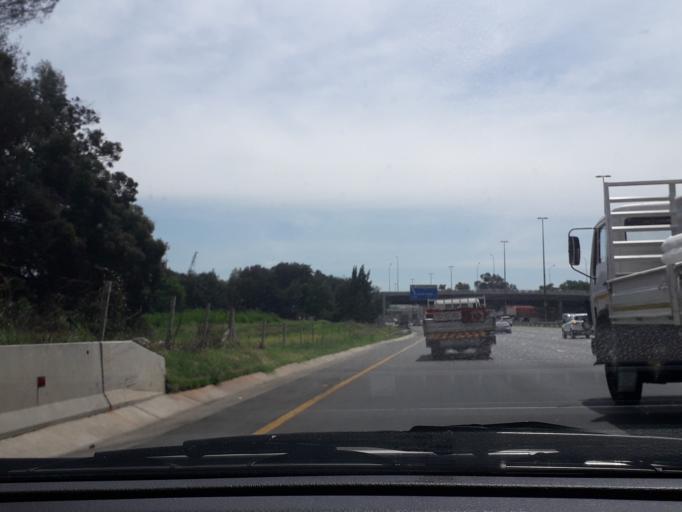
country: ZA
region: Gauteng
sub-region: City of Johannesburg Metropolitan Municipality
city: Roodepoort
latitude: -26.1807
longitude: 27.9452
